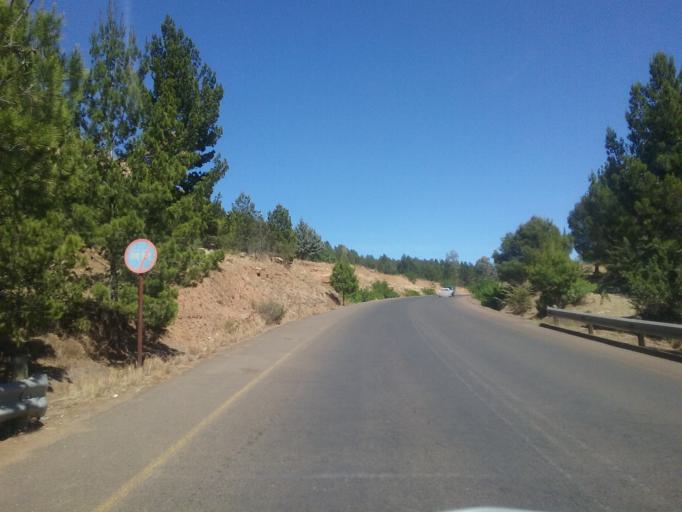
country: LS
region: Quthing
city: Quthing
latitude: -30.4033
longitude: 27.6775
